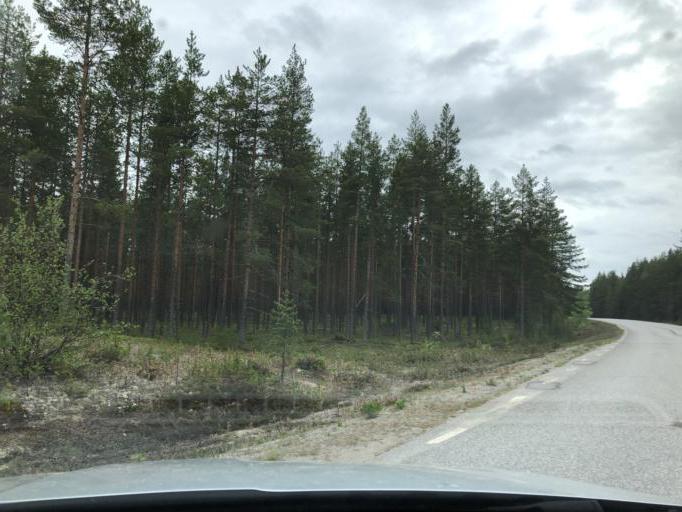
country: SE
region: Norrbotten
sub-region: Pitea Kommun
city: Pitea
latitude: 65.2380
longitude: 21.5198
